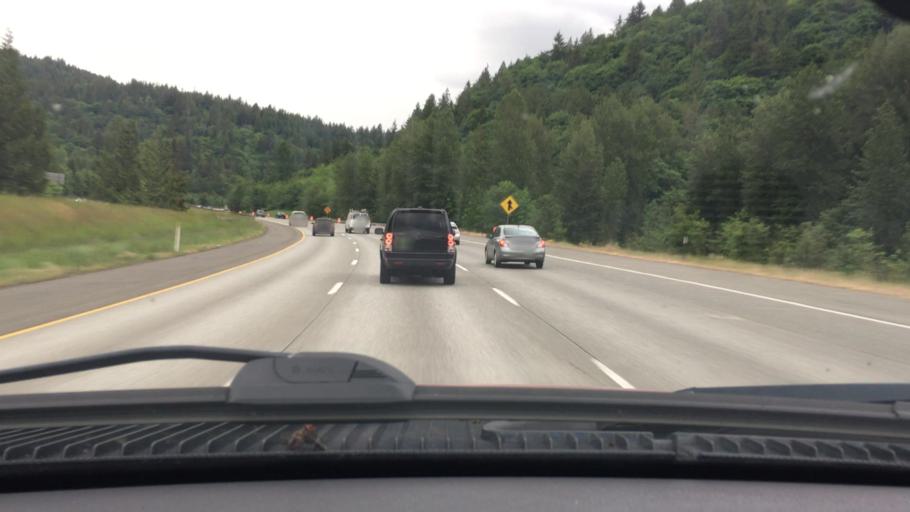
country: US
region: Washington
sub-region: King County
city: Issaquah
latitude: 47.5317
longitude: -121.9783
